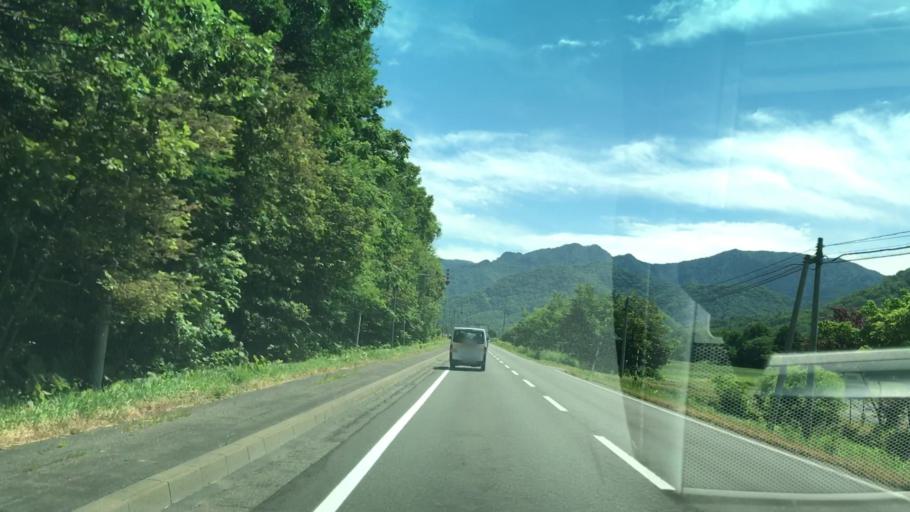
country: JP
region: Hokkaido
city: Shimo-furano
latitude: 42.8940
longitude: 142.5100
